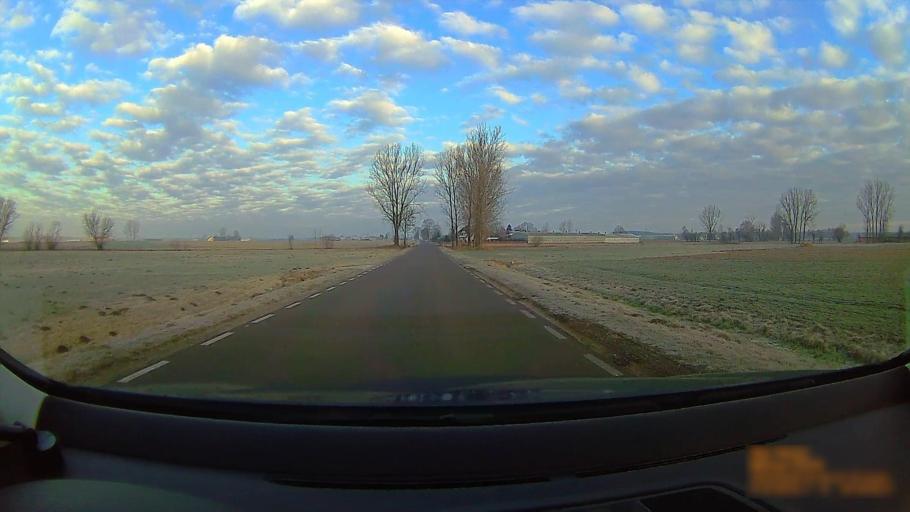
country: PL
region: Greater Poland Voivodeship
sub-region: Powiat koninski
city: Rzgow Pierwszy
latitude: 52.1072
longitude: 18.0820
